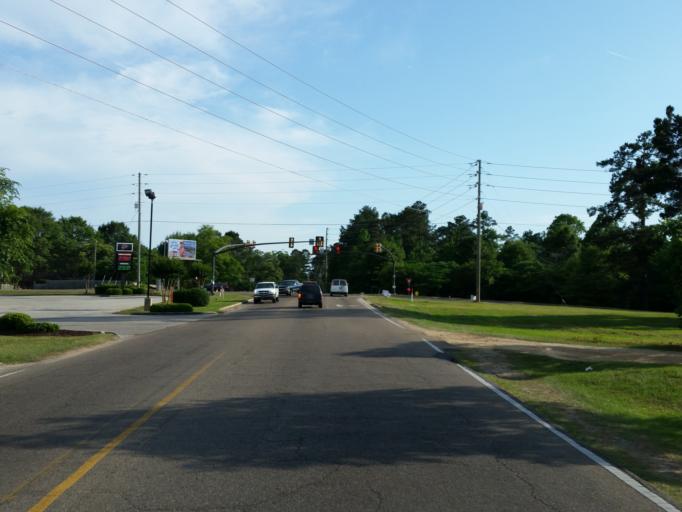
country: US
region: Mississippi
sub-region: Lamar County
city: West Hattiesburg
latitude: 31.3018
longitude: -89.3770
